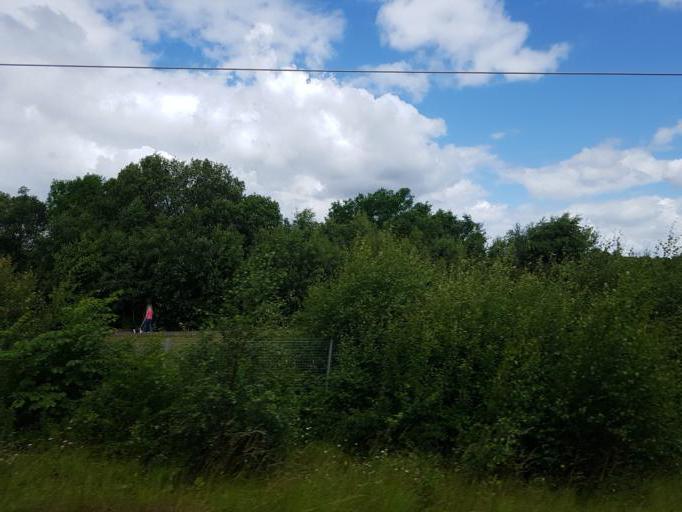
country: GB
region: Scotland
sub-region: West Lothian
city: Linlithgow
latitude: 55.9741
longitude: -3.6187
